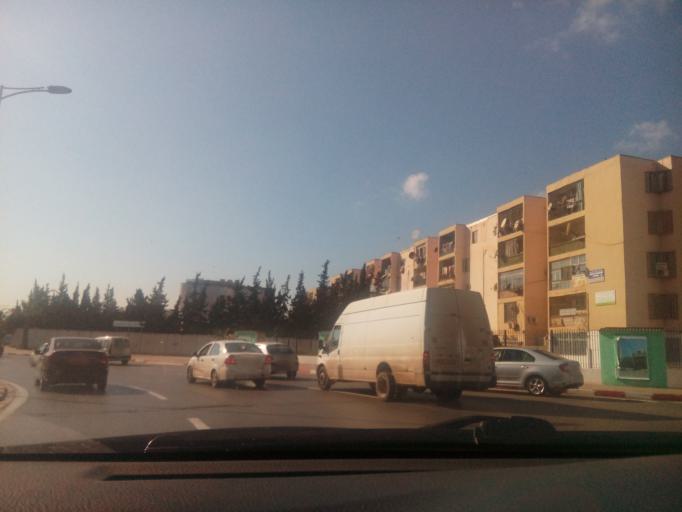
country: DZ
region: Oran
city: Oran
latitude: 35.7029
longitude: -0.5985
